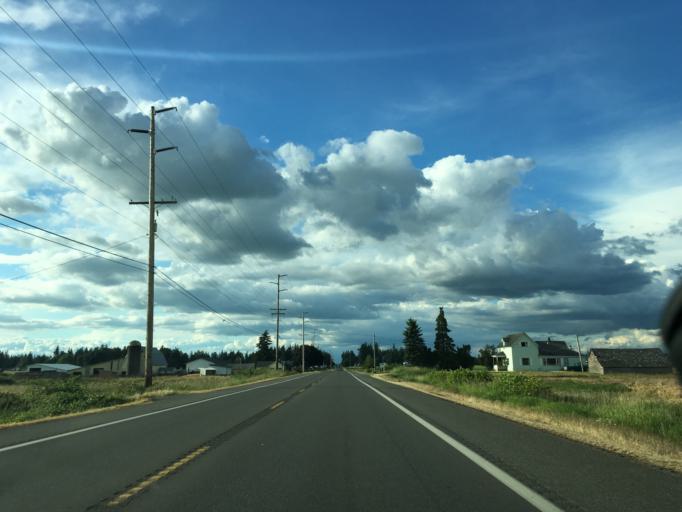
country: US
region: Washington
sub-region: Whatcom County
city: Lynden
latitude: 48.9014
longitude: -122.4422
